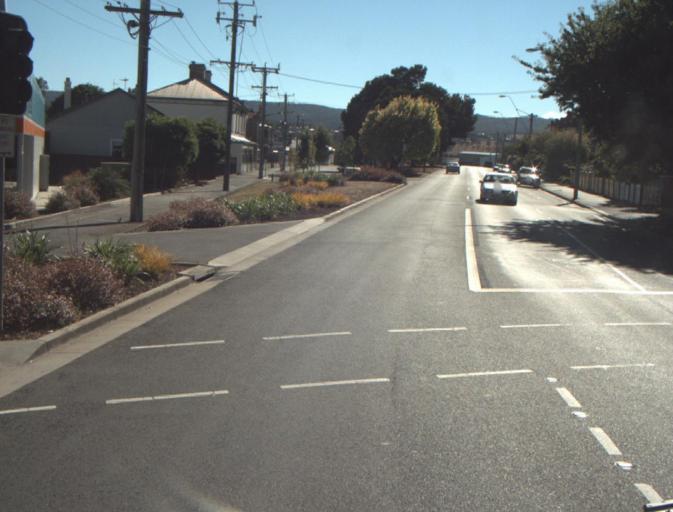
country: AU
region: Tasmania
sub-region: Launceston
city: East Launceston
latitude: -41.4312
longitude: 147.1443
